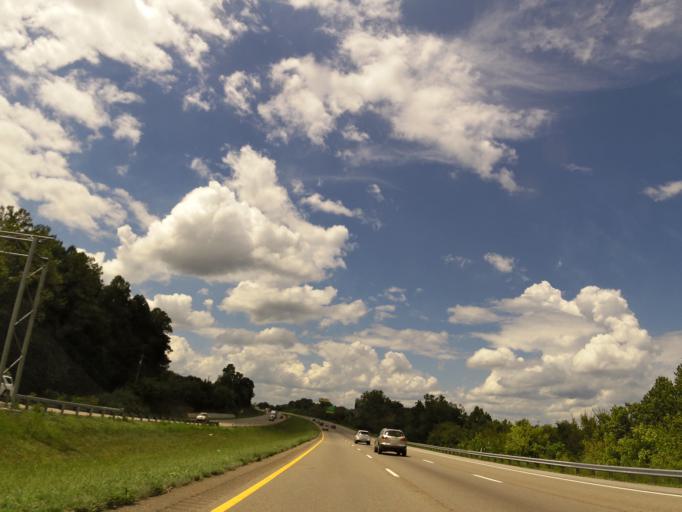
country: US
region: Tennessee
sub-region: Loudon County
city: Lenoir City
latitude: 35.8795
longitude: -84.3352
